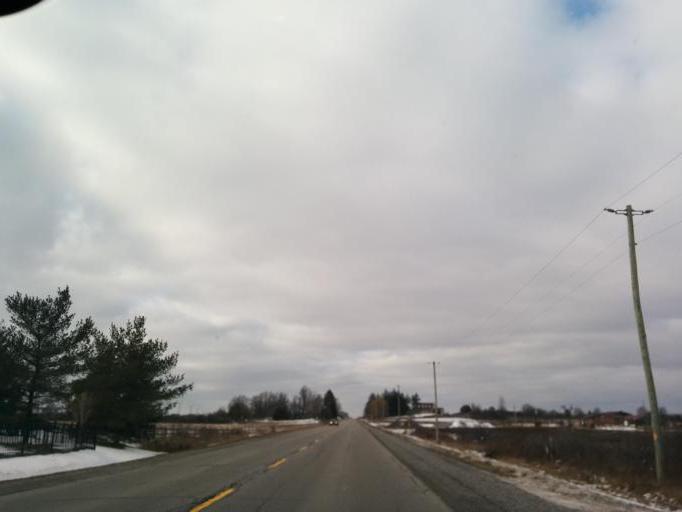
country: CA
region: Ontario
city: Brantford
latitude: 42.9775
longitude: -80.0937
